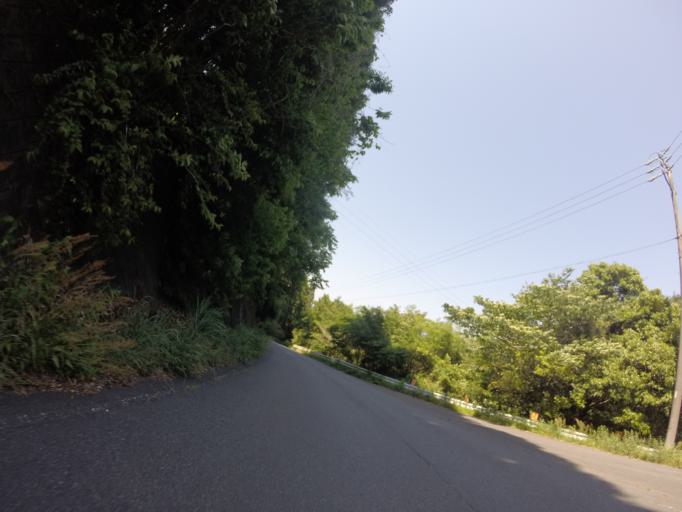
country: JP
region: Shizuoka
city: Fujinomiya
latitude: 35.1630
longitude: 138.5737
